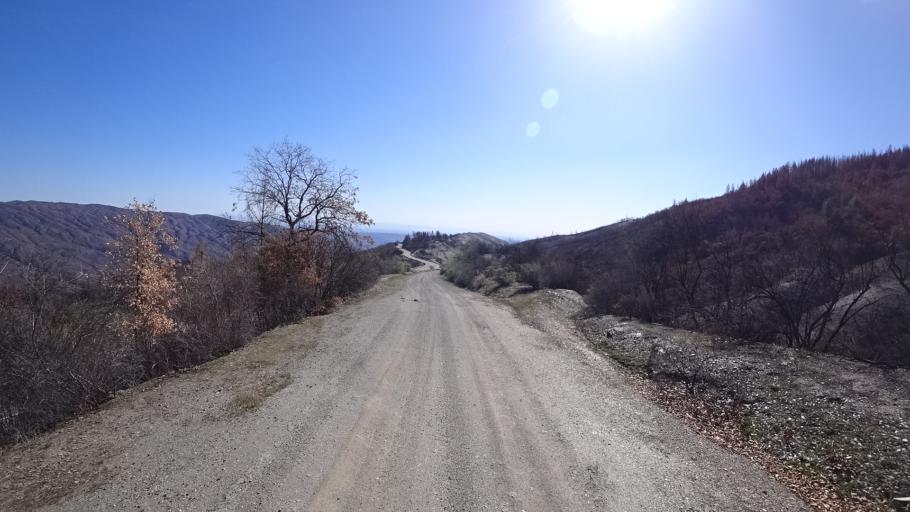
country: US
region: California
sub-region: Tehama County
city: Rancho Tehama Reserve
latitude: 39.6674
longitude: -122.6845
